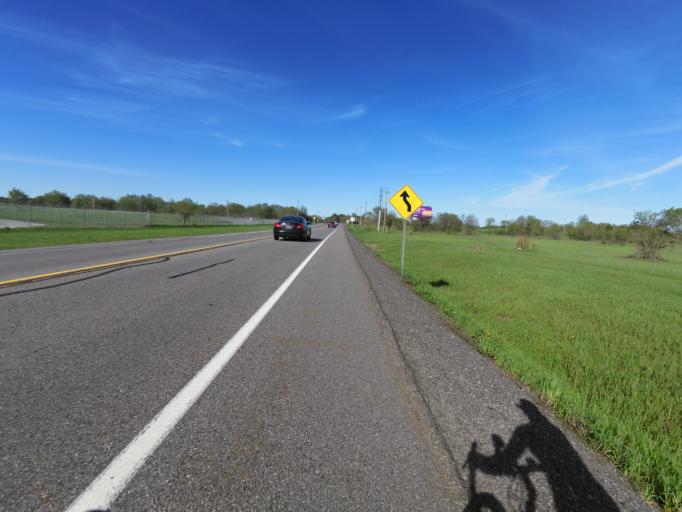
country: CA
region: Ontario
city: Ottawa
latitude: 45.3095
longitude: -75.6492
